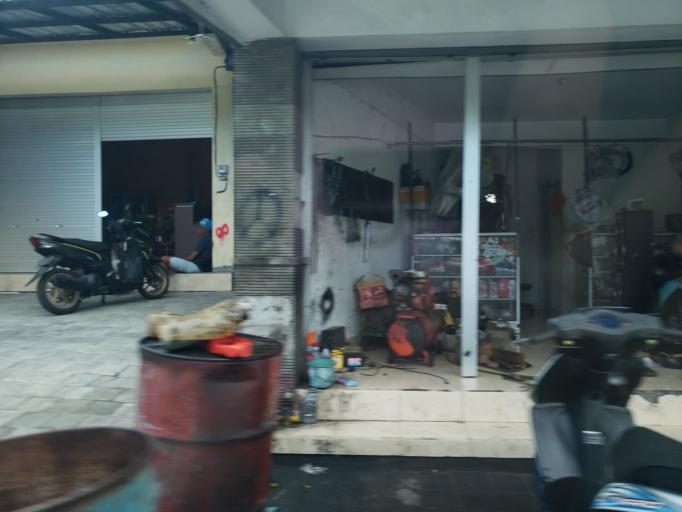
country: ID
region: Bali
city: Kangin
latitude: -8.8304
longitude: 115.1498
